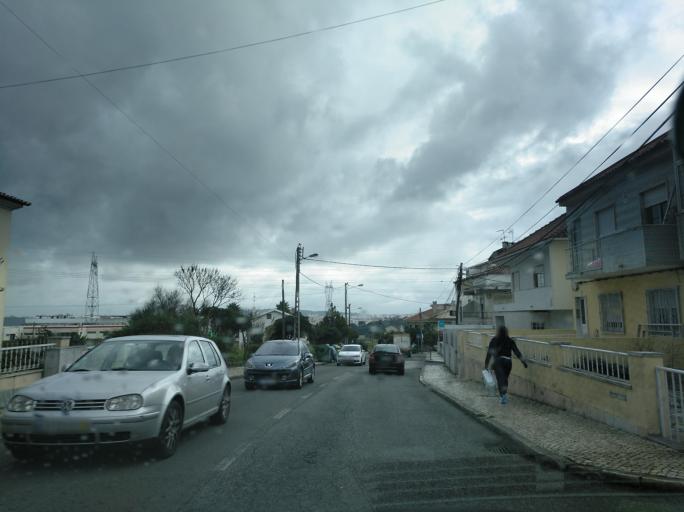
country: PT
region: Lisbon
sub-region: Odivelas
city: Famoes
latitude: 38.7880
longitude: -9.2093
